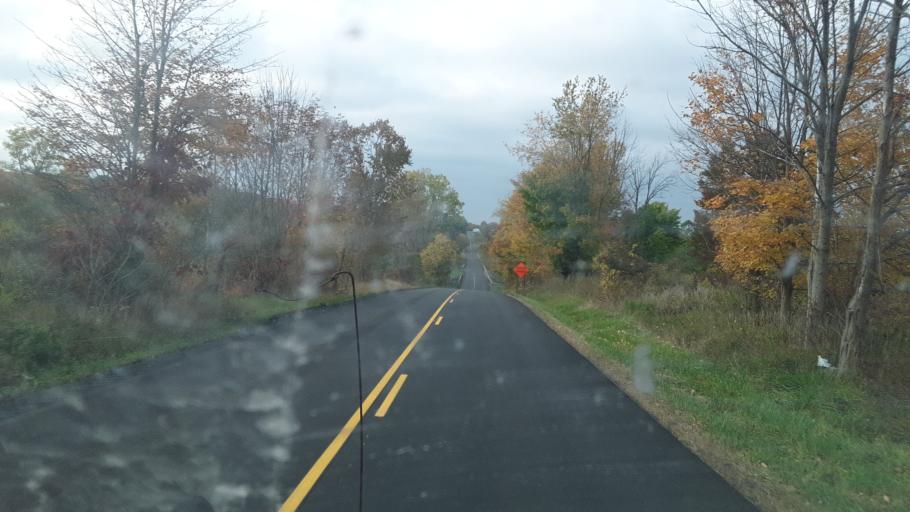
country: US
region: Ohio
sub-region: Ashland County
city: Loudonville
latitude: 40.7656
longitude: -82.2319
